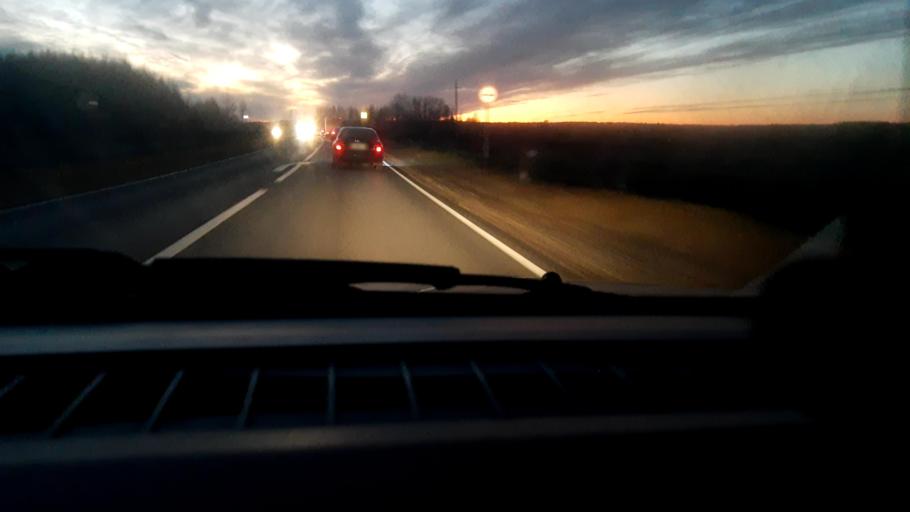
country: RU
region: Nizjnij Novgorod
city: Sukhobezvodnoye
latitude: 56.8537
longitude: 44.7700
